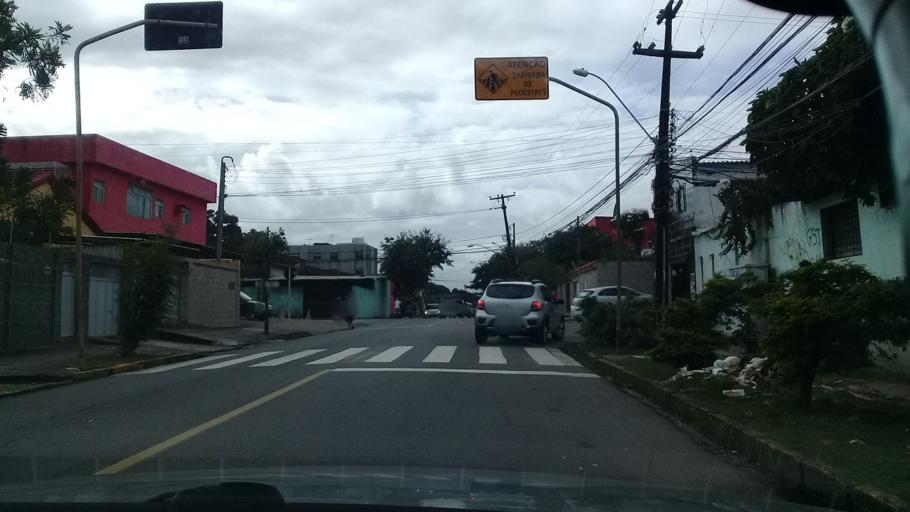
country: BR
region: Pernambuco
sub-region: Recife
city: Recife
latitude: -8.0371
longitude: -34.8798
